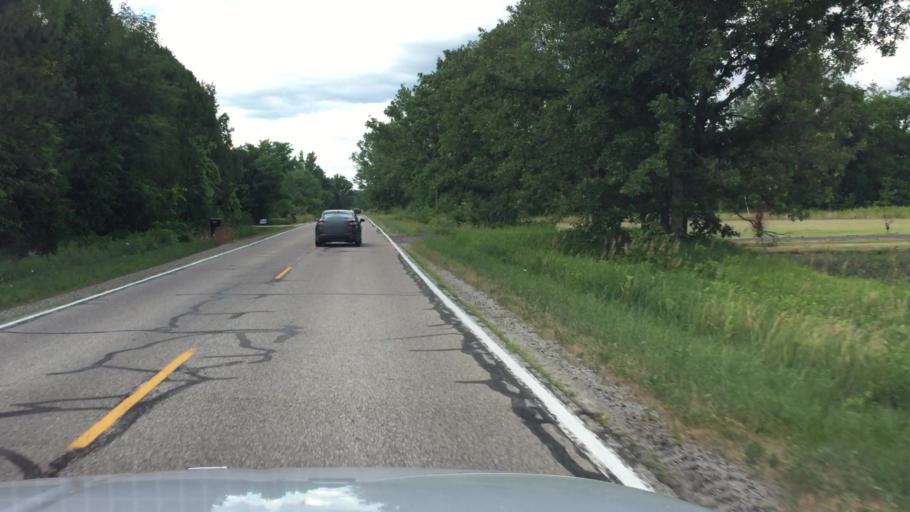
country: US
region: Michigan
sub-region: Saint Clair County
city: Yale
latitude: 43.1199
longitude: -82.8937
